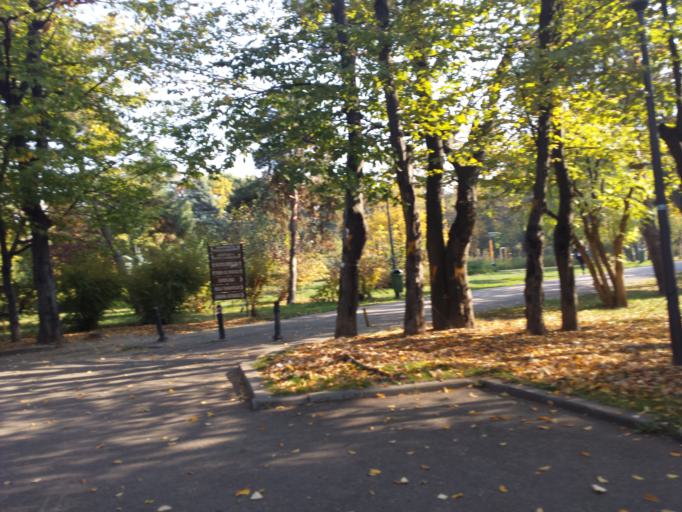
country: RO
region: Bucuresti
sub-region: Municipiul Bucuresti
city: Bucharest
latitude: 44.4722
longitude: 26.0855
